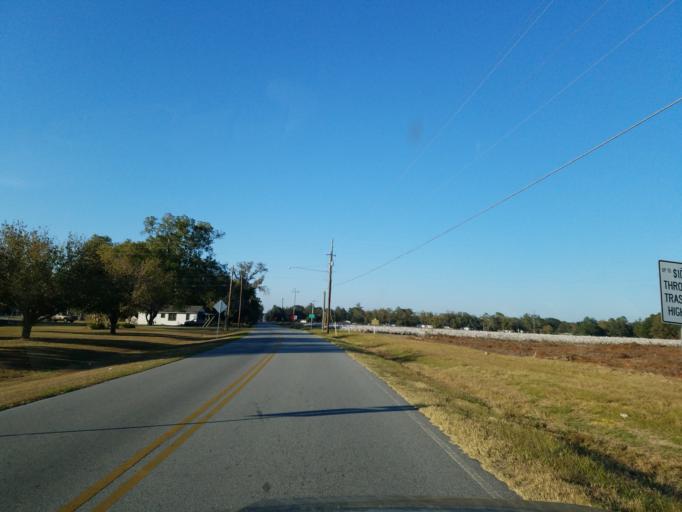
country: US
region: Georgia
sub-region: Lanier County
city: Lakeland
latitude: 31.0257
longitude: -83.0660
